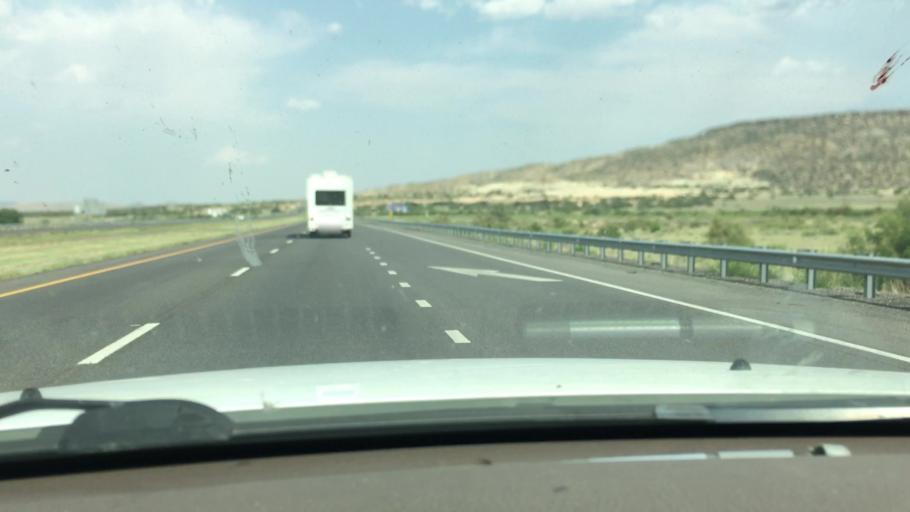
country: US
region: New Mexico
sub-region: Cibola County
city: Laguna
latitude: 35.0324
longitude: -107.4696
